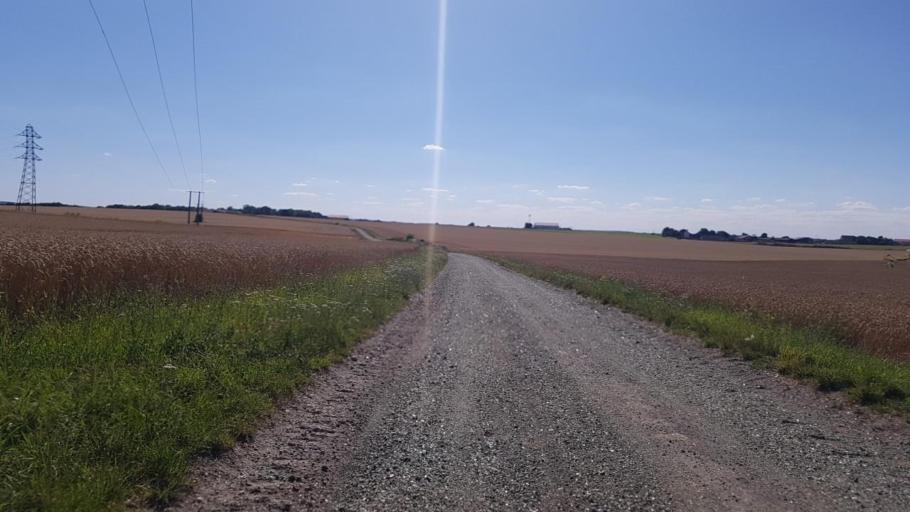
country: FR
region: Ile-de-France
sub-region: Departement de Seine-et-Marne
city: Chauconin-Neufmontiers
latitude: 48.9505
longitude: 2.8233
